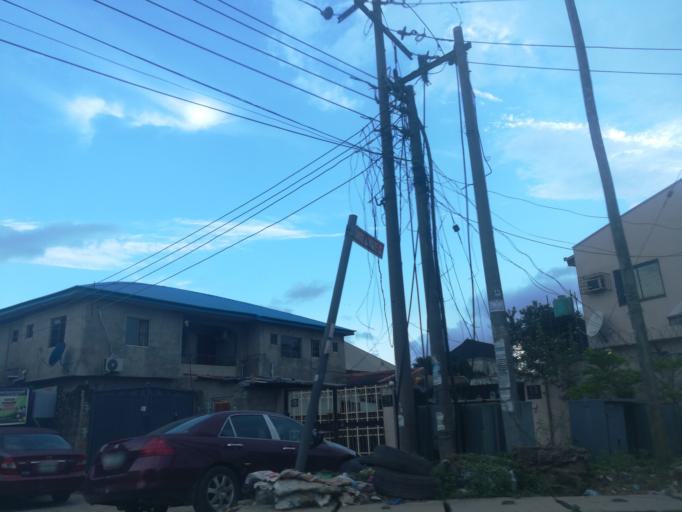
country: NG
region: Lagos
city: Somolu
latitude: 6.5546
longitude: 3.3861
